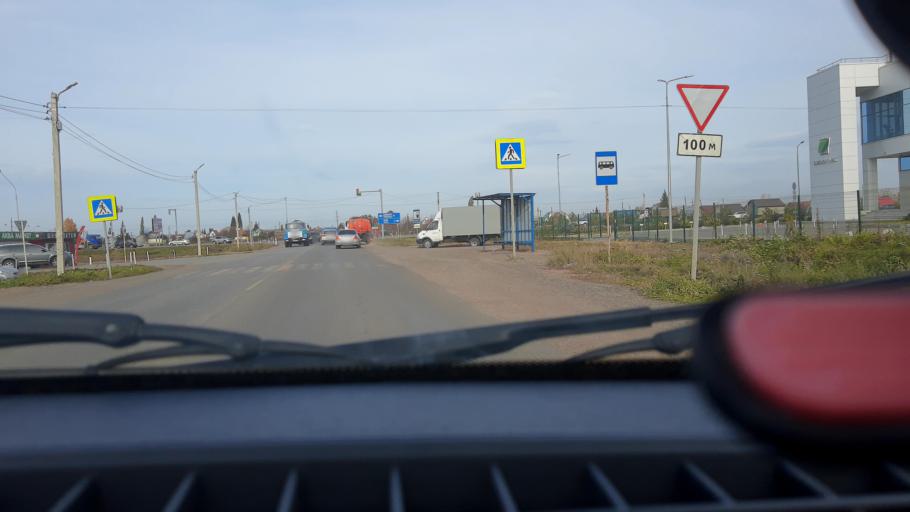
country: RU
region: Bashkortostan
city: Ufa
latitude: 54.6325
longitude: 55.9206
